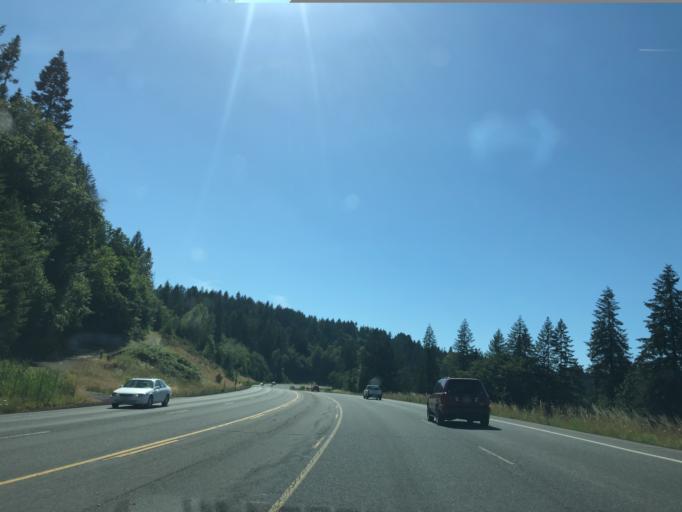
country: US
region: Oregon
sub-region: Linn County
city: Sweet Home
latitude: 44.4049
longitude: -122.7526
